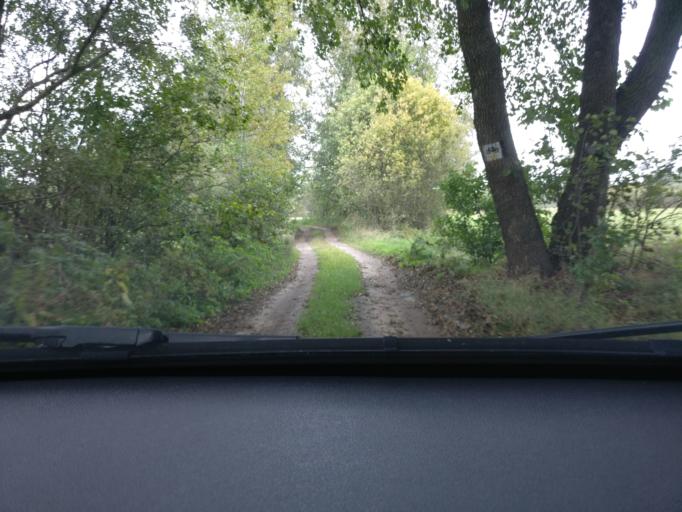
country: PL
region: Masovian Voivodeship
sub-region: Powiat kozienicki
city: Garbatka-Letnisko
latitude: 51.5204
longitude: 21.6000
